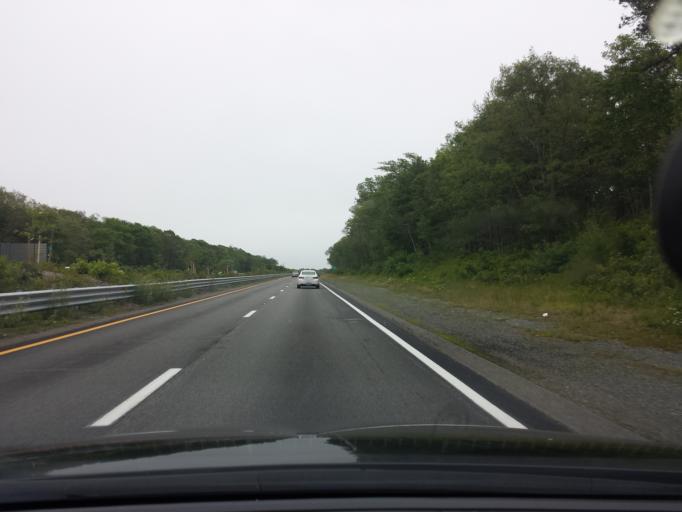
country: US
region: Massachusetts
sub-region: Barnstable County
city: East Sandwich
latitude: 41.7376
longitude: -70.4779
